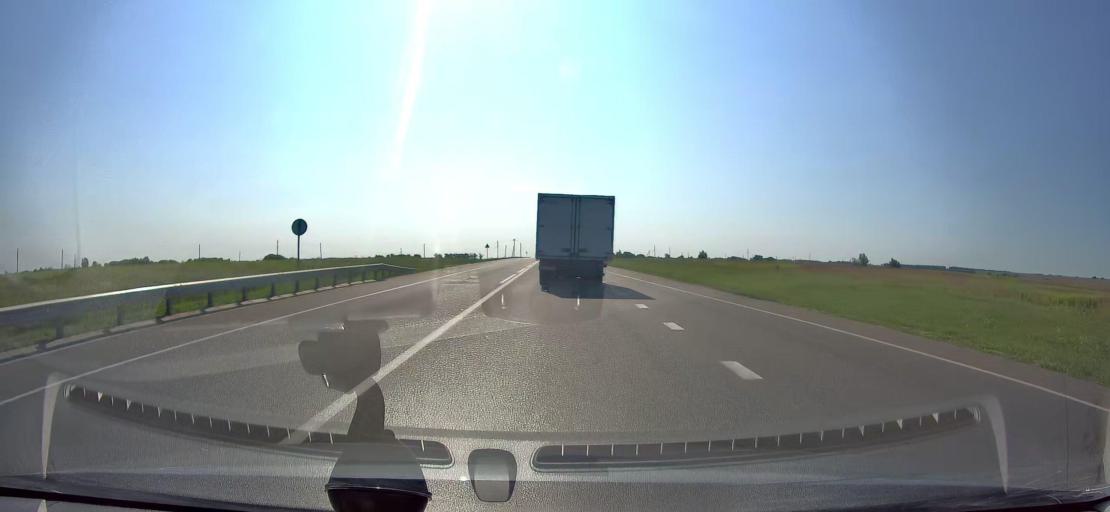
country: RU
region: Orjol
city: Kromy
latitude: 52.6542
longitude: 35.7228
